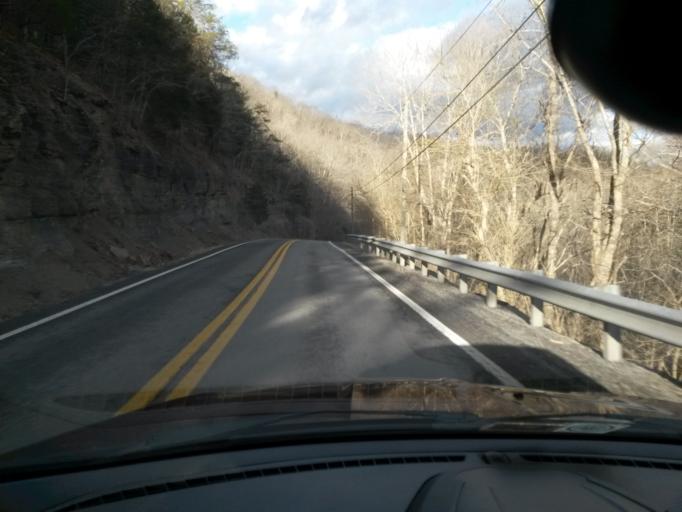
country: US
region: West Virginia
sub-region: Monroe County
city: Union
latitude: 37.5251
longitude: -80.6120
